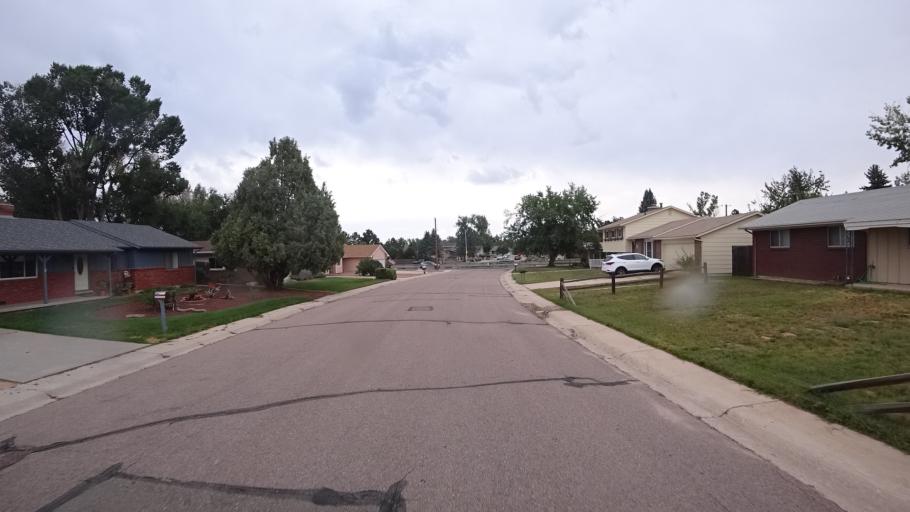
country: US
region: Colorado
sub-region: El Paso County
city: Colorado Springs
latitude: 38.9247
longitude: -104.8015
